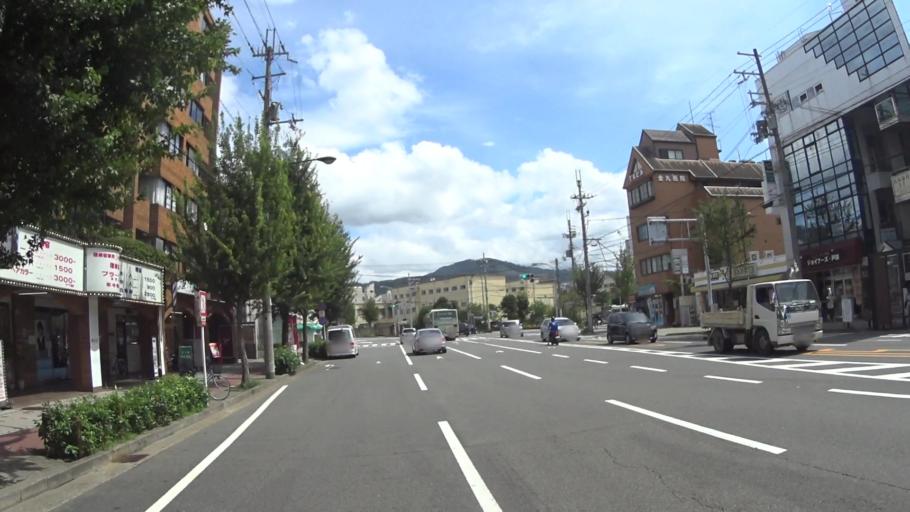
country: JP
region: Kyoto
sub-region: Kyoto-shi
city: Kamigyo-ku
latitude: 35.0413
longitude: 135.7819
